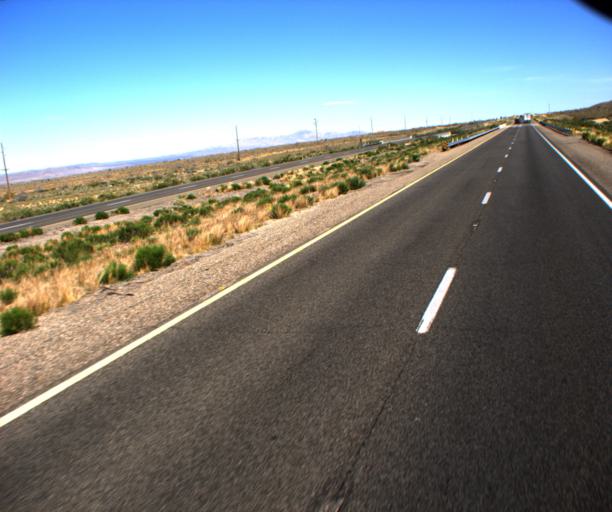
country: US
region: Arizona
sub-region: Mohave County
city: Dolan Springs
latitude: 35.4110
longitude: -114.2694
